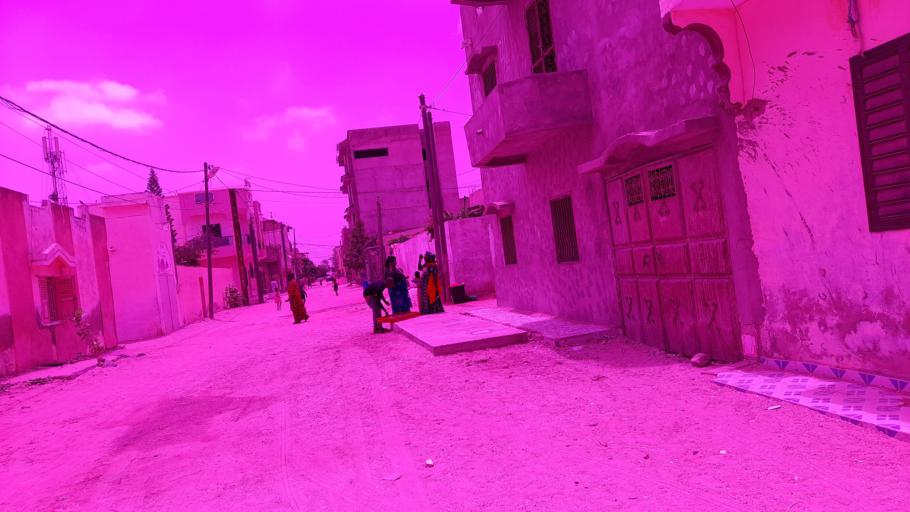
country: SN
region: Saint-Louis
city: Saint-Louis
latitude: 16.0177
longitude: -16.4870
